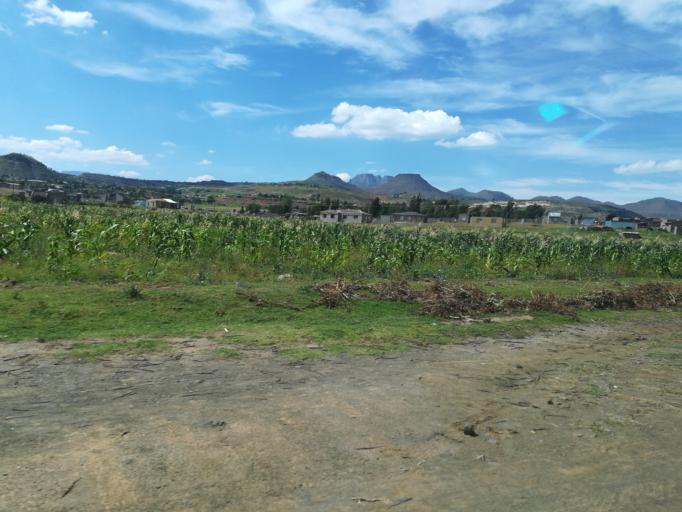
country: LS
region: Mohale's Hoek District
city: Mohale's Hoek
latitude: -30.1072
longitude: 27.4672
